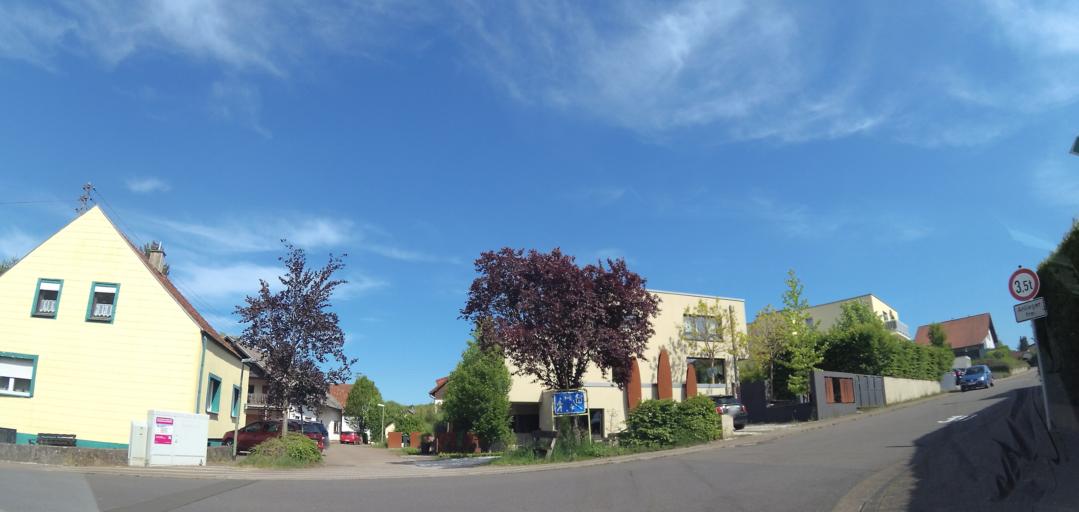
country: DE
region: Saarland
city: Losheim
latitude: 49.4488
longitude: 6.7637
